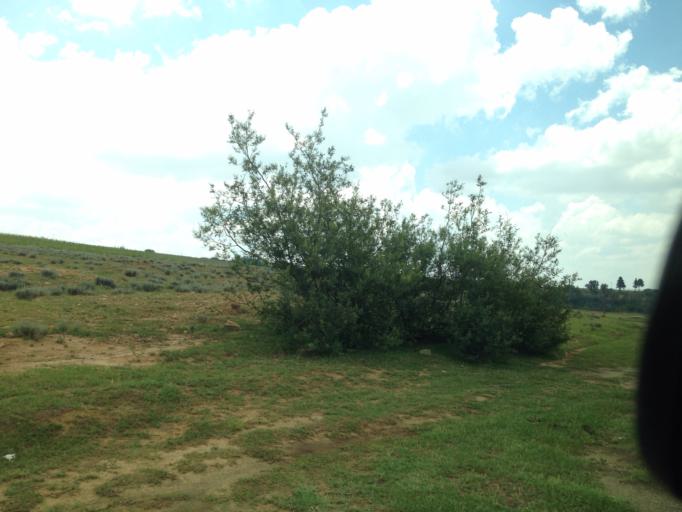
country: LS
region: Maseru
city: Maseru
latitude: -29.4579
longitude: 27.5645
